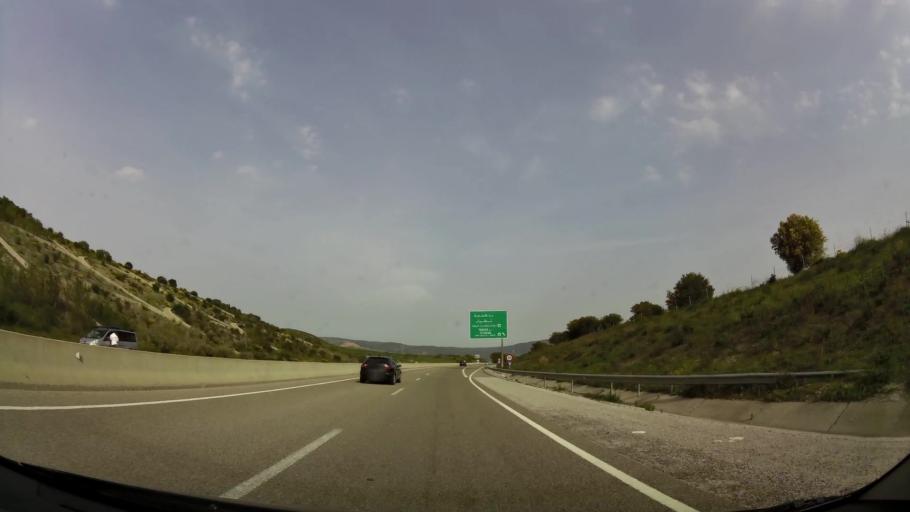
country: MA
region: Tanger-Tetouan
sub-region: Tanger-Assilah
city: Tangier
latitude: 35.6841
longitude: -5.7131
